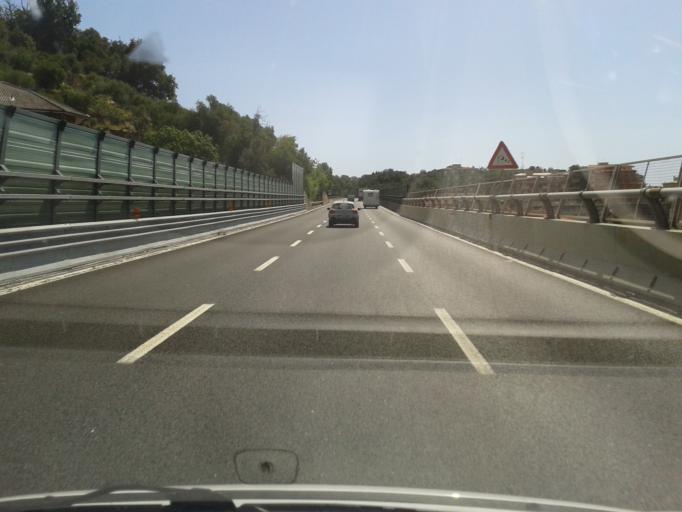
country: IT
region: Liguria
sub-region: Provincia di Savona
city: Varazze
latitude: 44.3639
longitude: 8.5760
